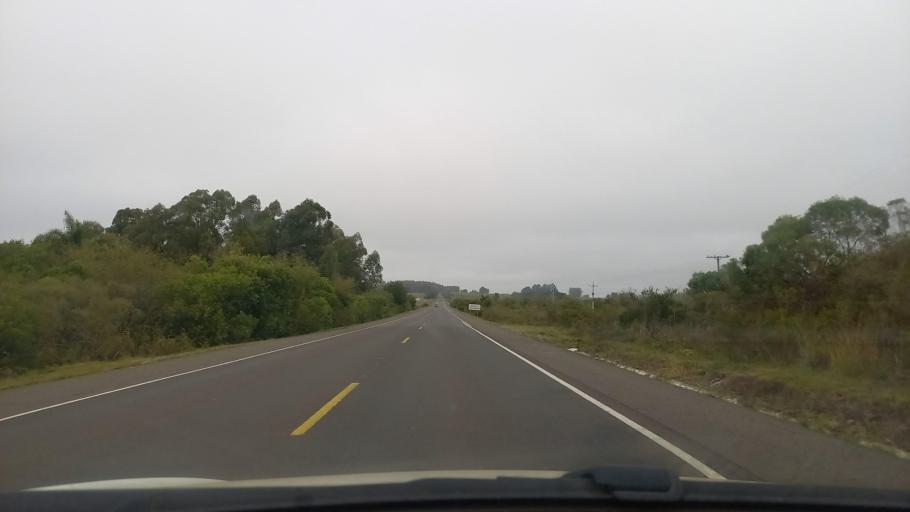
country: BR
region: Rio Grande do Sul
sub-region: Rosario Do Sul
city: Rosario do Sul
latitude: -30.3109
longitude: -54.9962
